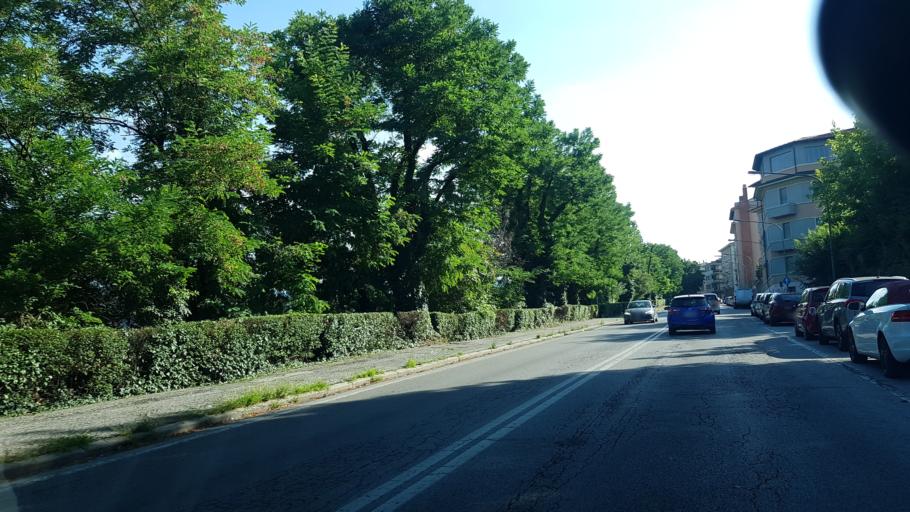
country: IT
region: Piedmont
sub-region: Provincia di Cuneo
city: Cuneo
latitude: 44.3891
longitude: 7.5517
